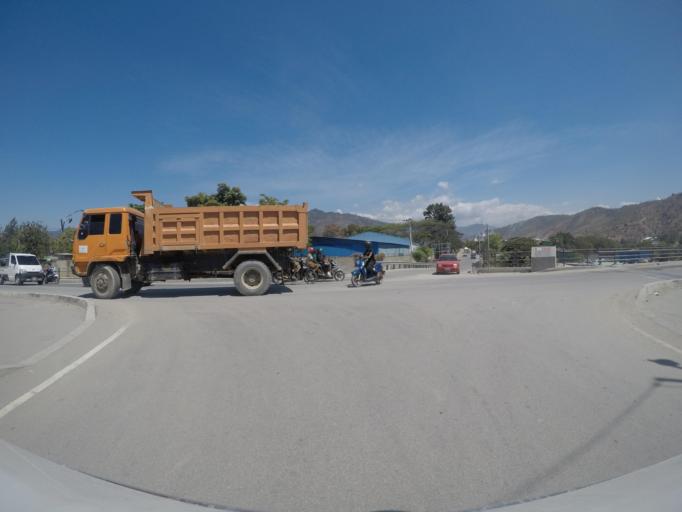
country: TL
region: Dili
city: Dili
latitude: -8.5608
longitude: 125.5349
